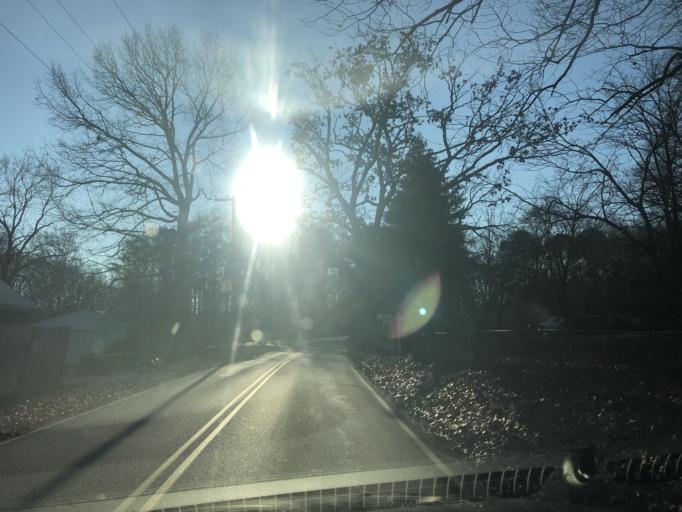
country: US
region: Maryland
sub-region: Anne Arundel County
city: Odenton
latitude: 39.0774
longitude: -76.7101
